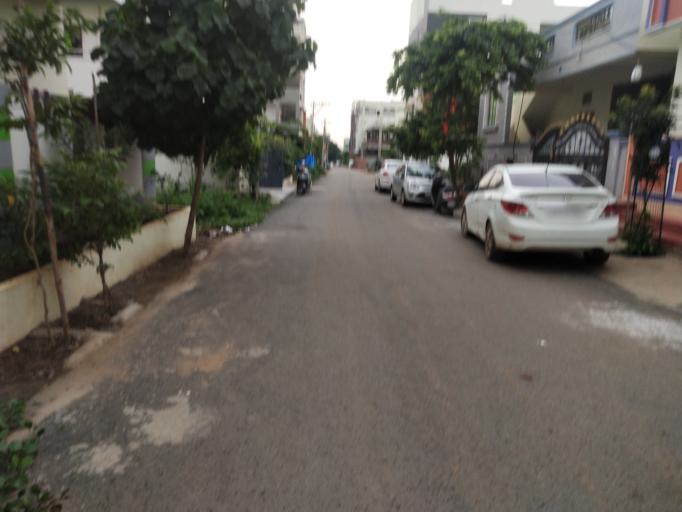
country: IN
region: Telangana
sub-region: Rangareddi
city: Lal Bahadur Nagar
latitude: 17.3243
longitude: 78.5403
